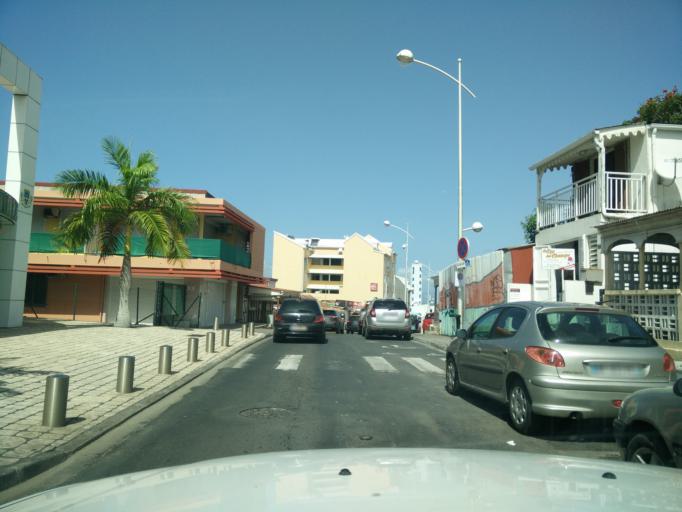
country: GP
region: Guadeloupe
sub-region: Guadeloupe
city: Le Gosier
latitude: 16.2062
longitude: -61.4920
